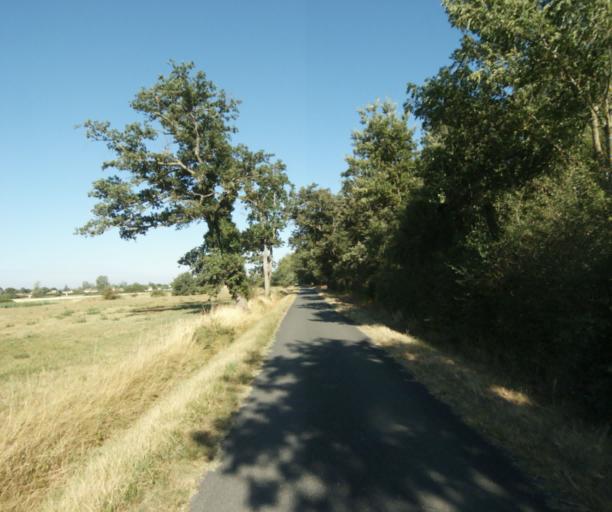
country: FR
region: Midi-Pyrenees
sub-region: Departement de la Haute-Garonne
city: Revel
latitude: 43.4624
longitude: 2.0231
